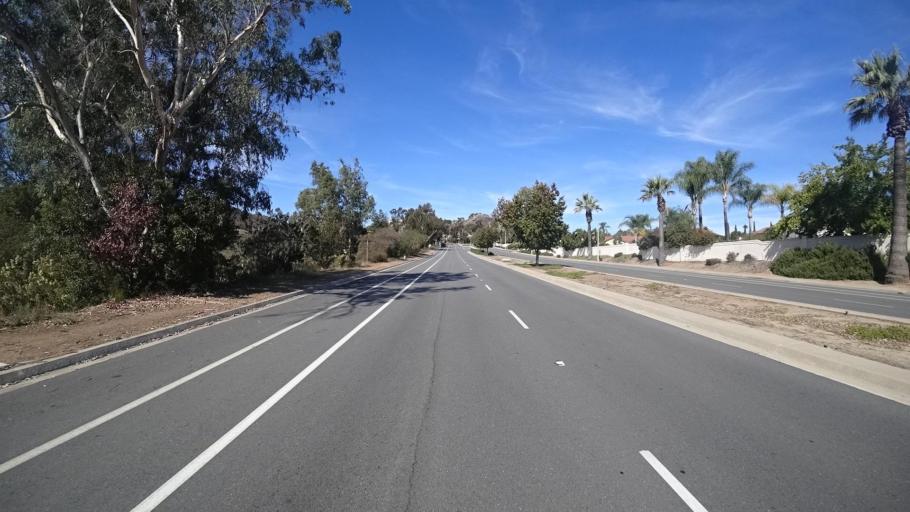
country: US
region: California
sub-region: San Diego County
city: Rancho San Diego
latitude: 32.7489
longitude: -116.9392
